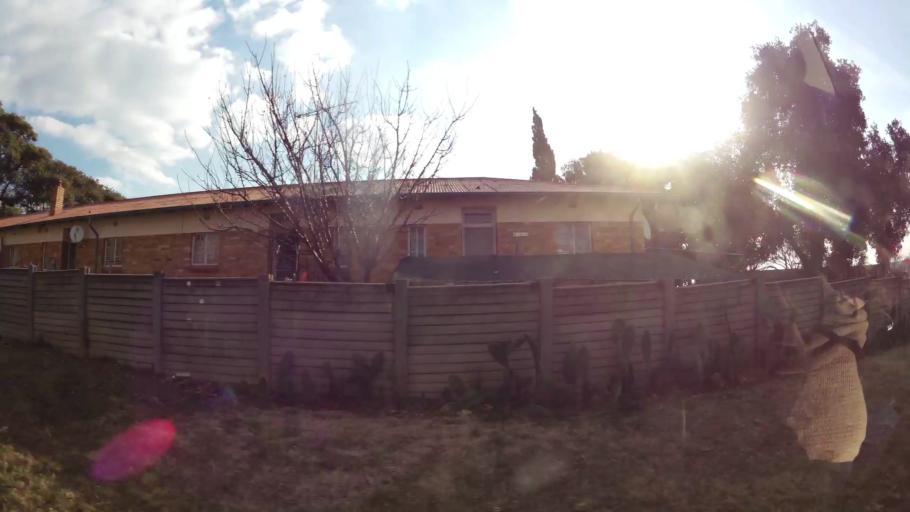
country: ZA
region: Gauteng
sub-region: West Rand District Municipality
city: Krugersdorp
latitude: -26.1011
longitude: 27.7625
